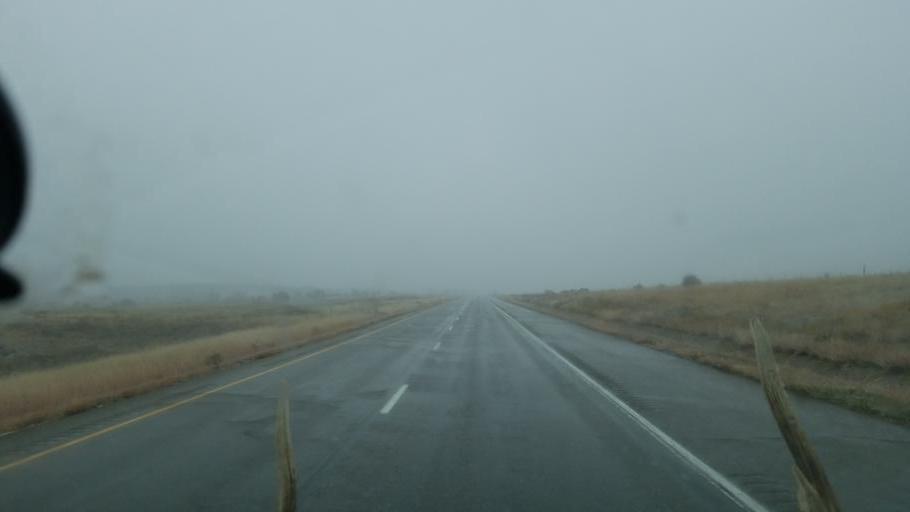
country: US
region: Colorado
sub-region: Pueblo County
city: Colorado City
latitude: 38.0496
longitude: -104.7237
